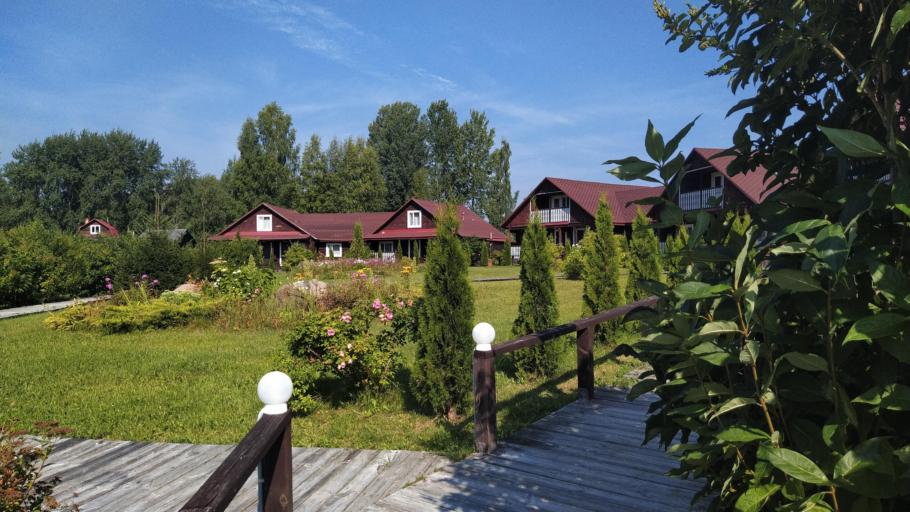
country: RU
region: Pskov
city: Pushkinskiye Gory
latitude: 56.9827
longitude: 29.0034
